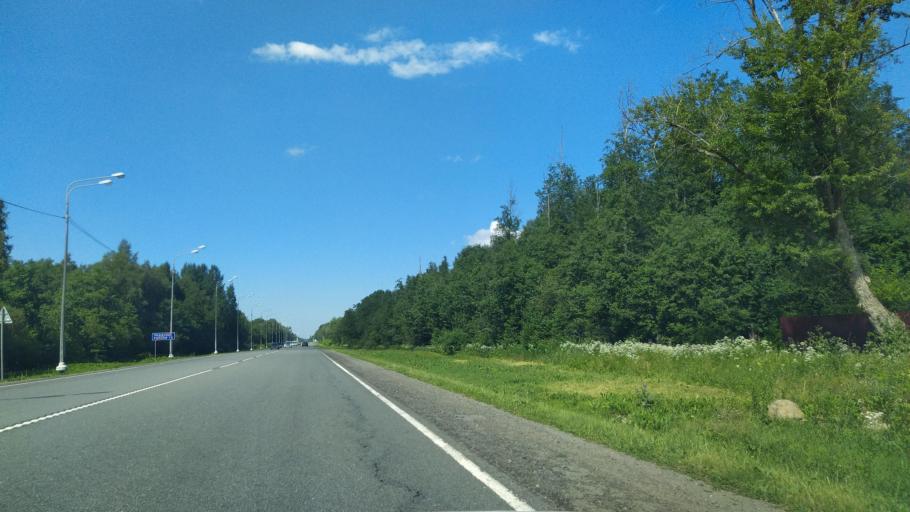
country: RU
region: Leningrad
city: Rozhdestveno
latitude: 59.3748
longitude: 29.9669
